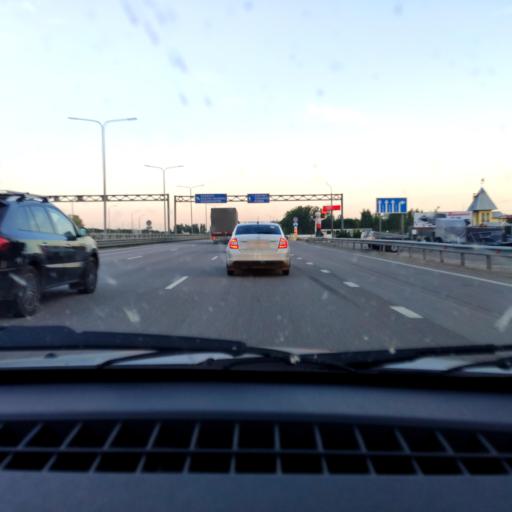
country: RU
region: Voronezj
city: Podgornoye
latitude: 51.8451
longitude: 39.2116
